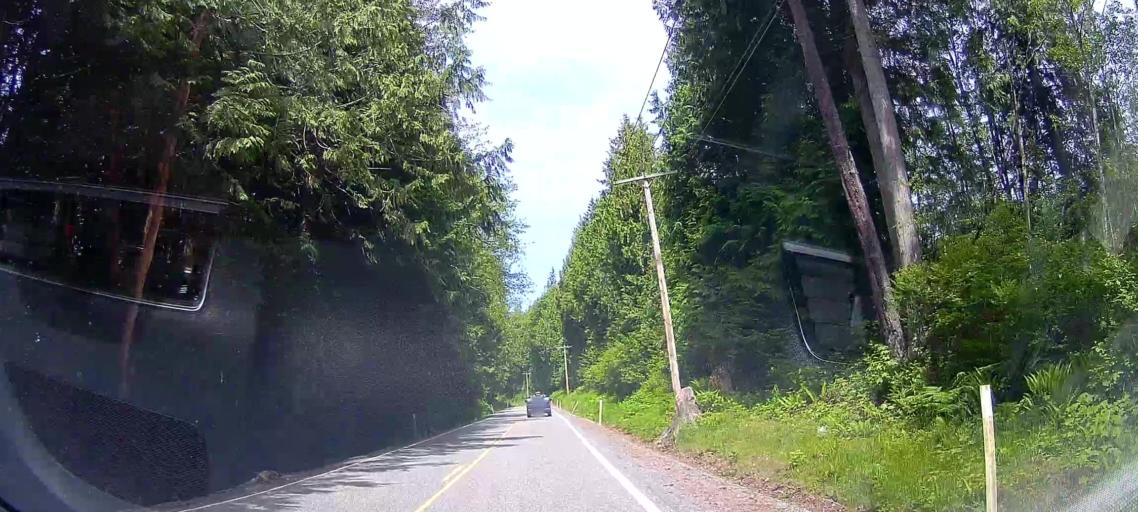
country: US
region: Washington
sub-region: Snohomish County
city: Bryant
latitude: 48.3349
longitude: -122.1680
